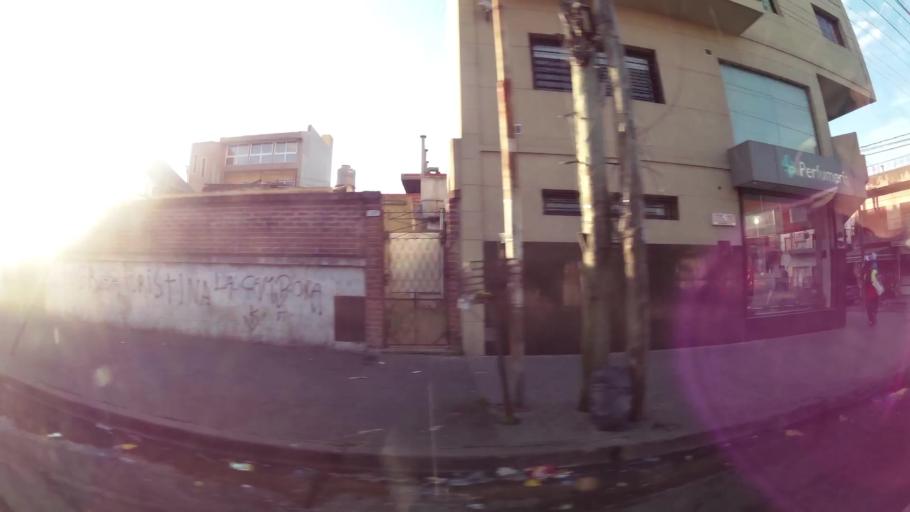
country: AR
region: Buenos Aires F.D.
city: Villa Lugano
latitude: -34.6941
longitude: -58.4850
